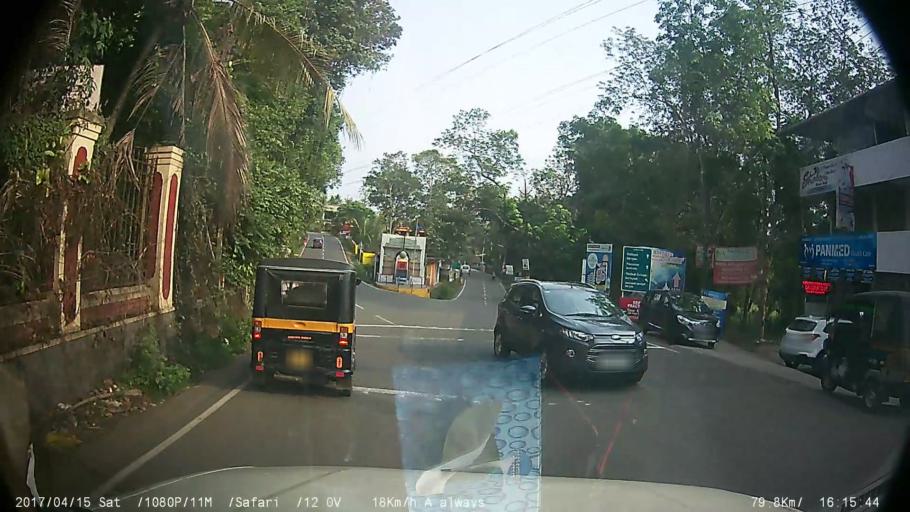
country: IN
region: Kerala
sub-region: Kottayam
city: Kottayam
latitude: 9.6601
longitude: 76.5297
